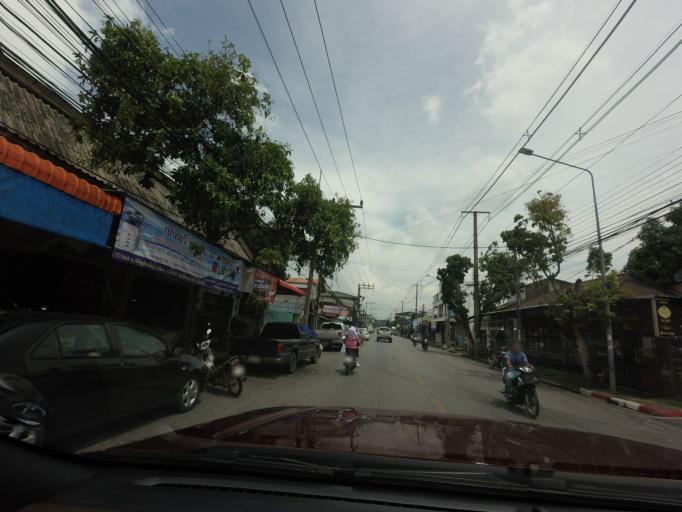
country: TH
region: Yala
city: Yala
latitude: 6.5332
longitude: 101.2856
